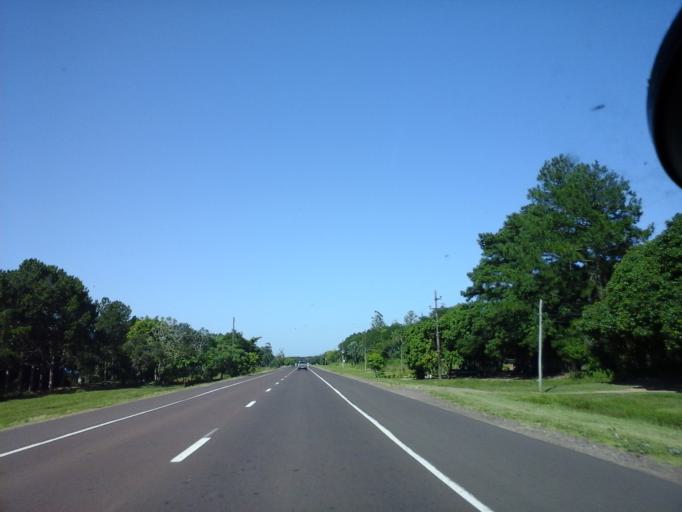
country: AR
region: Corrientes
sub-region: Departamento de San Cosme
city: San Cosme
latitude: -27.3863
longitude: -58.5427
